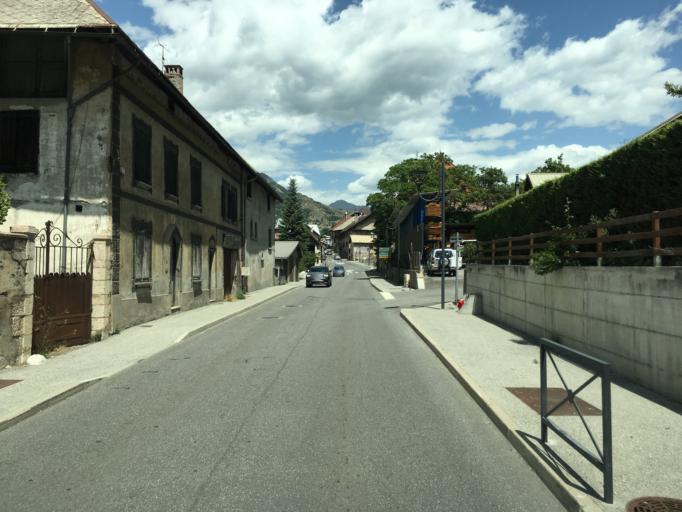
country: FR
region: Provence-Alpes-Cote d'Azur
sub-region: Departement des Hautes-Alpes
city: Saint-Martin-de-Queyrieres
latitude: 44.7930
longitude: 6.5623
